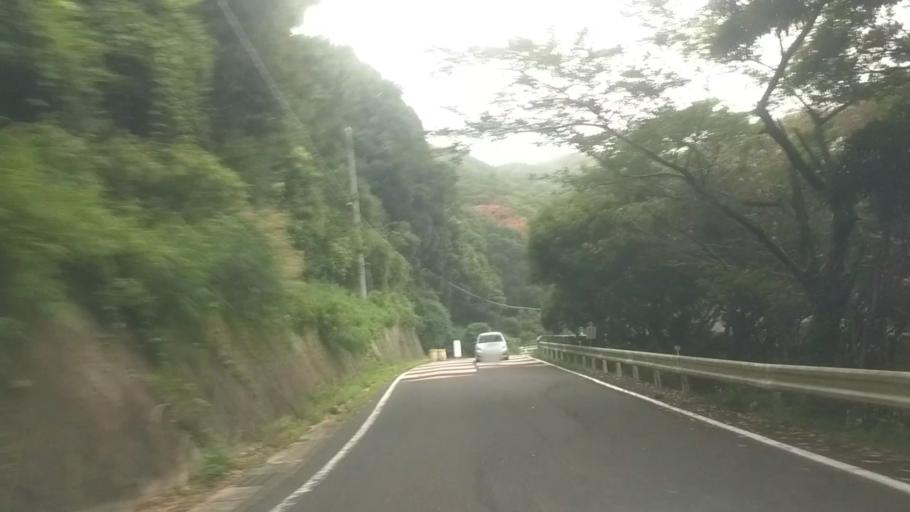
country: JP
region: Chiba
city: Kawaguchi
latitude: 35.1408
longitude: 140.1500
